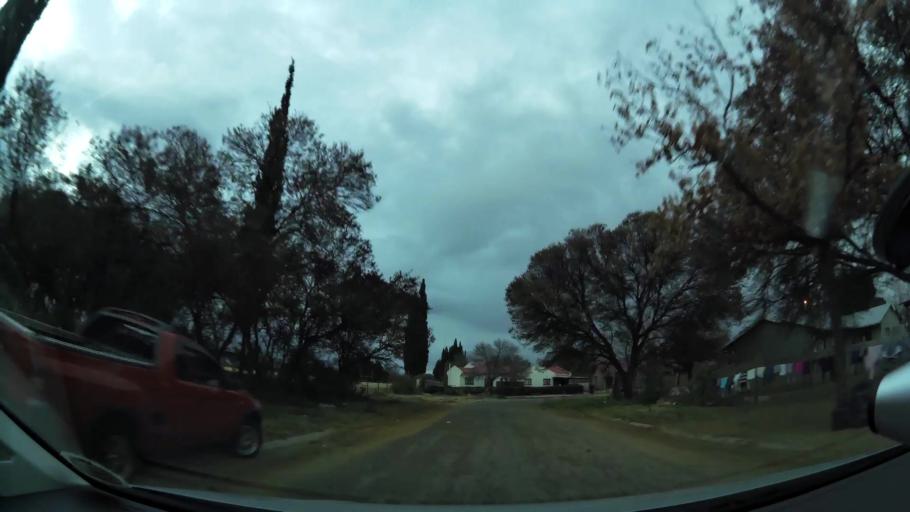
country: ZA
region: Orange Free State
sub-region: Lejweleputswa District Municipality
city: Welkom
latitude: -27.9783
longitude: 26.7484
